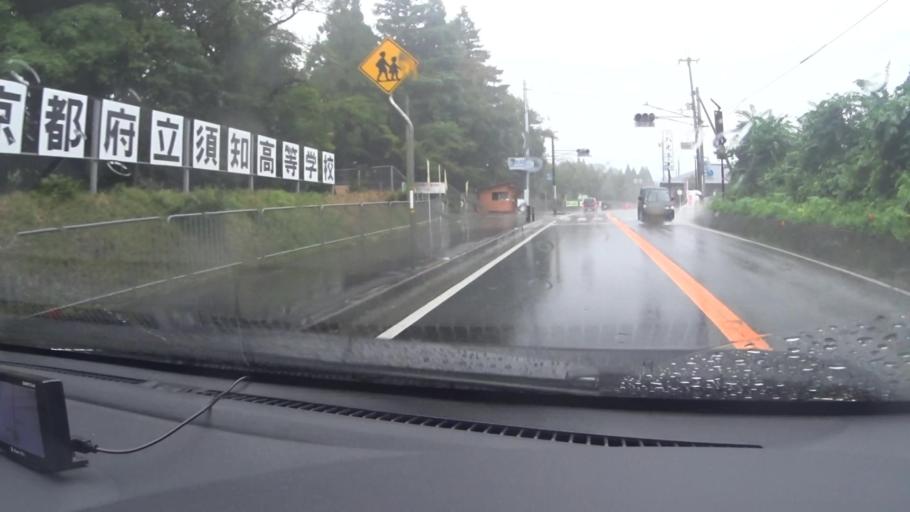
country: JP
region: Kyoto
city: Ayabe
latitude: 35.1722
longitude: 135.4142
